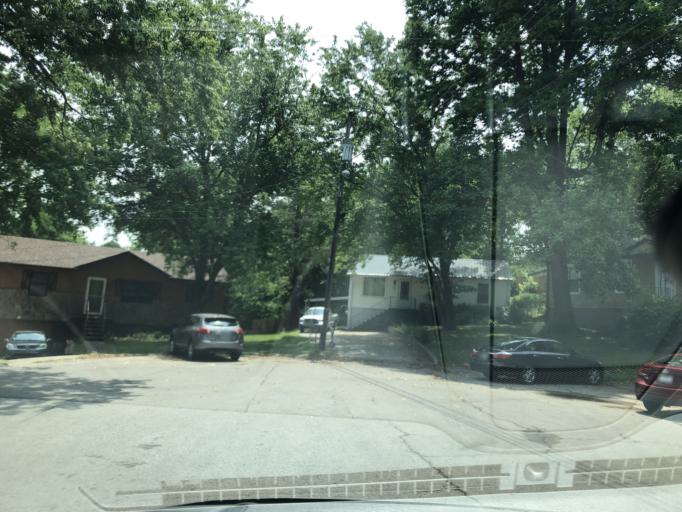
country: US
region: Tennessee
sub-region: Davidson County
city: Oak Hill
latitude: 36.0629
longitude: -86.6861
